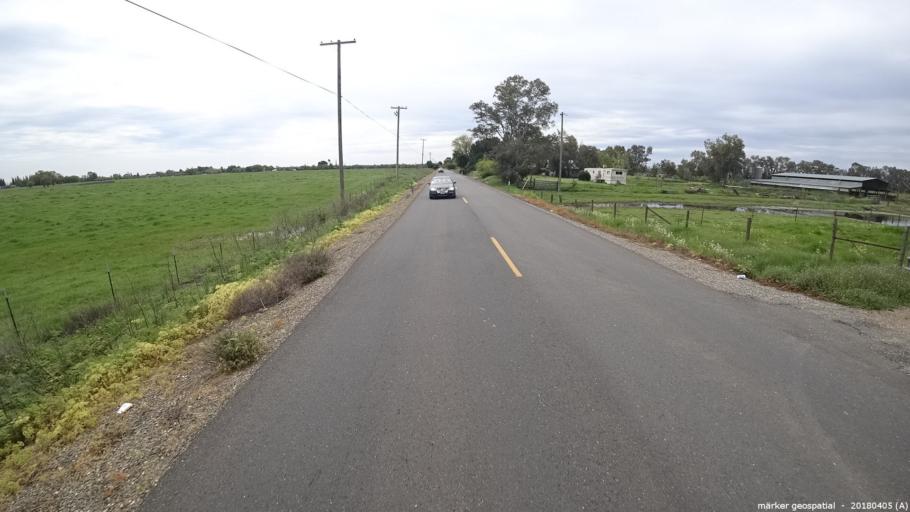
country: US
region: California
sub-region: Sacramento County
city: Galt
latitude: 38.2889
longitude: -121.3375
